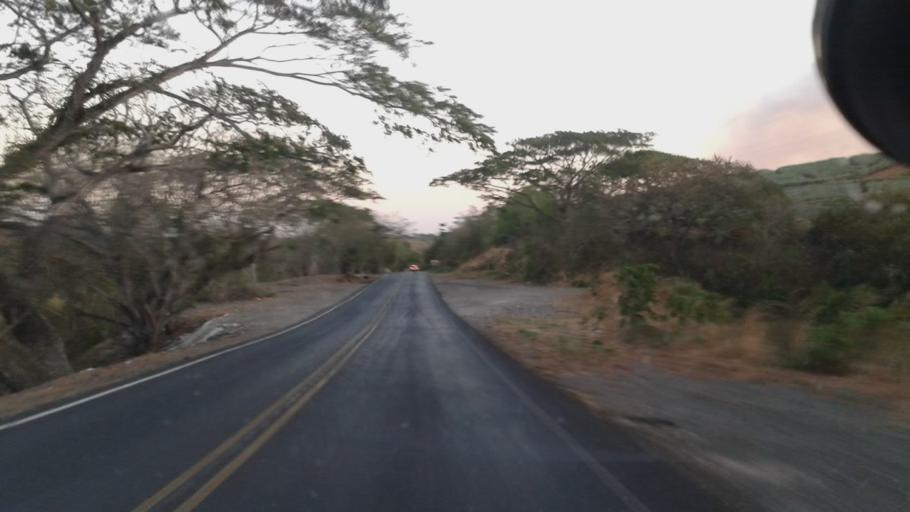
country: CR
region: Puntarenas
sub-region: Canton Central de Puntarenas
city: Puntarenas
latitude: 10.0936
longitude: -84.8553
